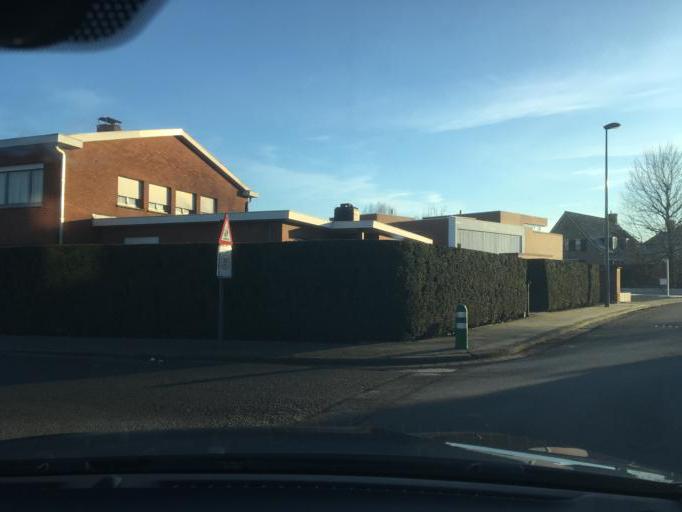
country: BE
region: Flanders
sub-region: Provincie West-Vlaanderen
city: Ardooie
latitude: 50.9755
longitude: 3.1993
